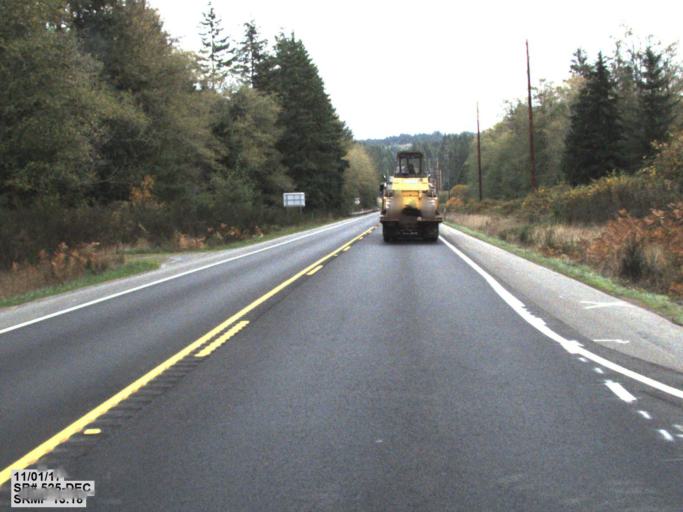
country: US
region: Washington
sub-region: Island County
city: Langley
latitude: 48.0038
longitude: -122.4346
